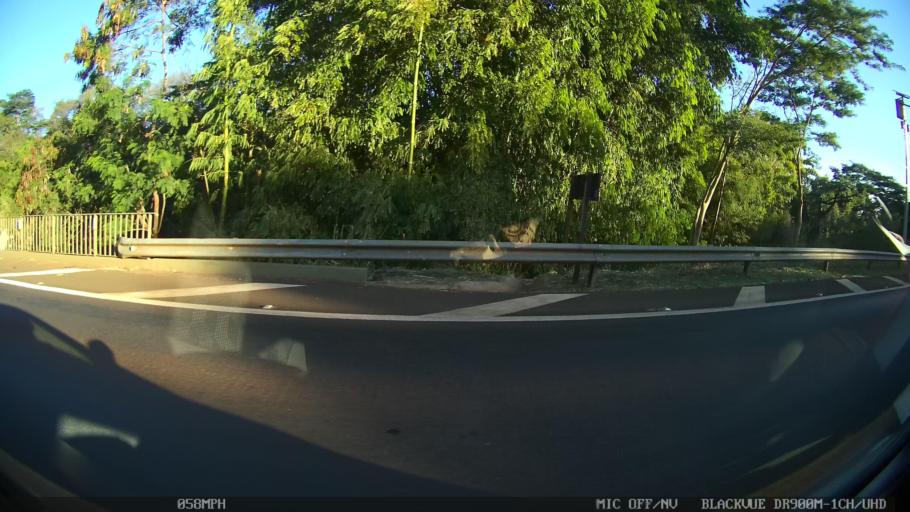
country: BR
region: Sao Paulo
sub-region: Araraquara
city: Araraquara
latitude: -21.8173
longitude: -48.1894
